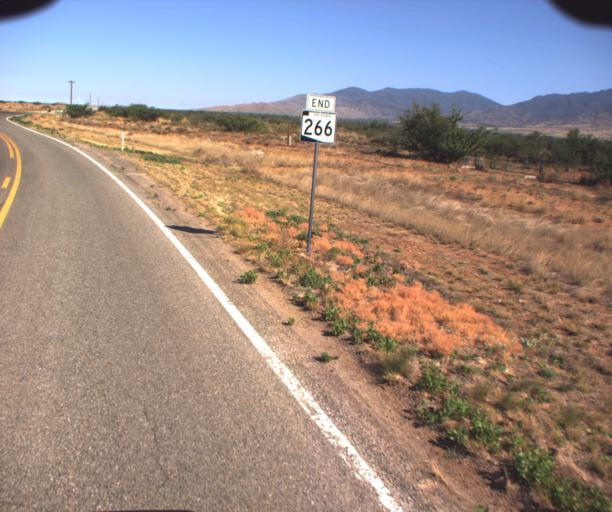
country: US
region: Arizona
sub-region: Graham County
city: Swift Trail Junction
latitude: 32.5898
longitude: -109.9689
